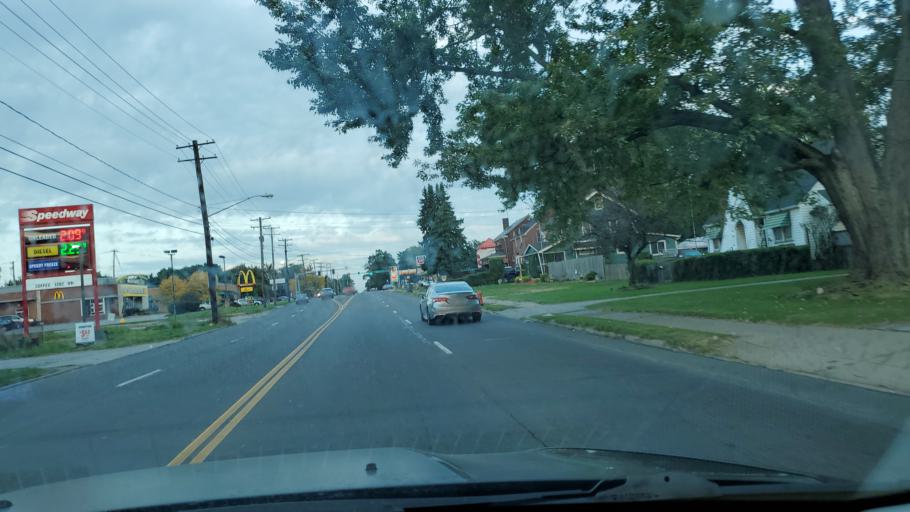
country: US
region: Ohio
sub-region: Mahoning County
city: Struthers
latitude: 41.0608
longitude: -80.6426
